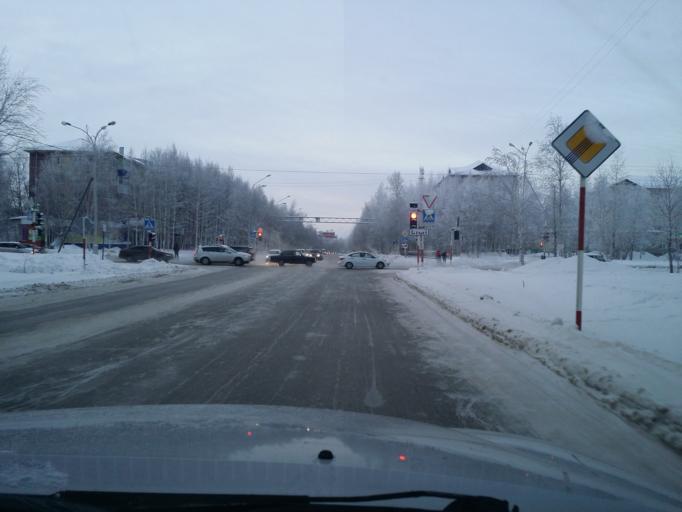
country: RU
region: Khanty-Mansiyskiy Avtonomnyy Okrug
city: Nizhnevartovsk
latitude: 60.9359
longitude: 76.5750
